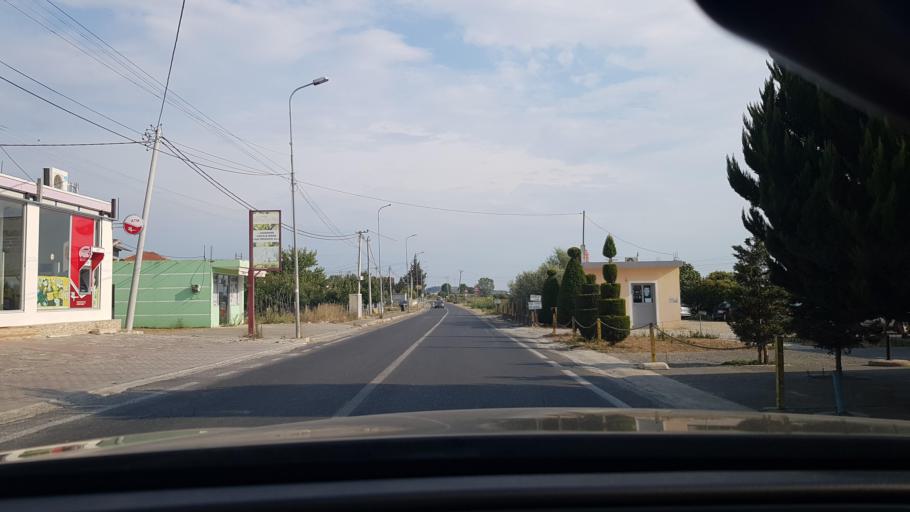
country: AL
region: Durres
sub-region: Rrethi i Durresit
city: Manze
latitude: 41.4630
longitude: 19.5635
